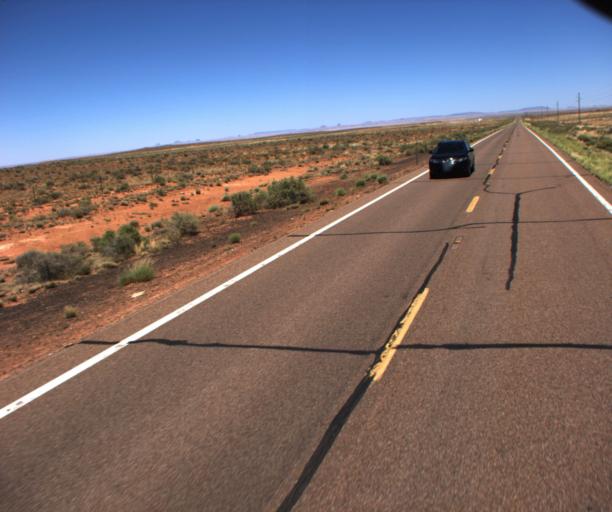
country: US
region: Arizona
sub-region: Coconino County
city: LeChee
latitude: 34.9467
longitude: -110.7690
